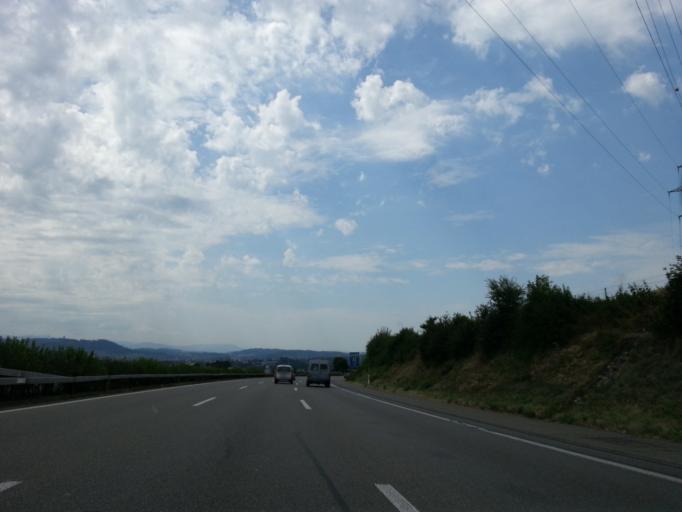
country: CH
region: Bern
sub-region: Bern-Mittelland District
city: Bolligen
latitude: 46.9926
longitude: 7.4822
